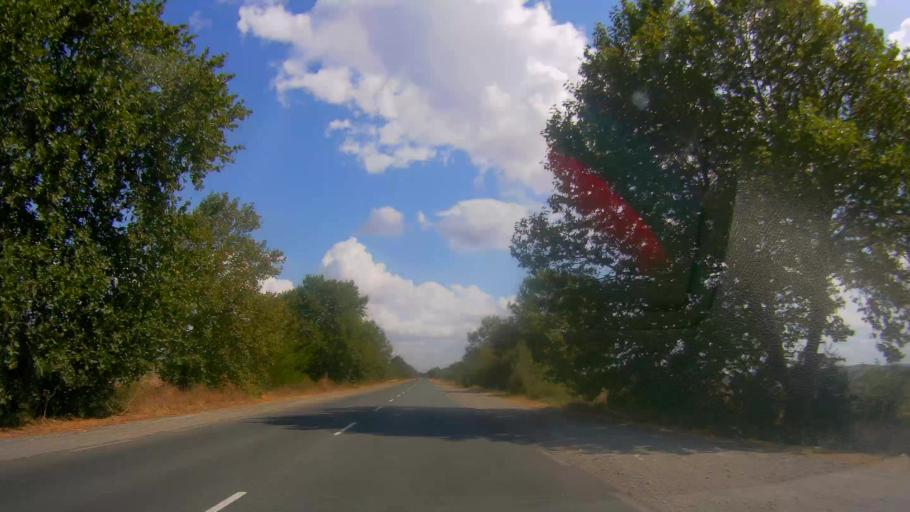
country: BG
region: Sliven
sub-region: Obshtina Sliven
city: Kermen
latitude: 42.6345
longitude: 26.1615
